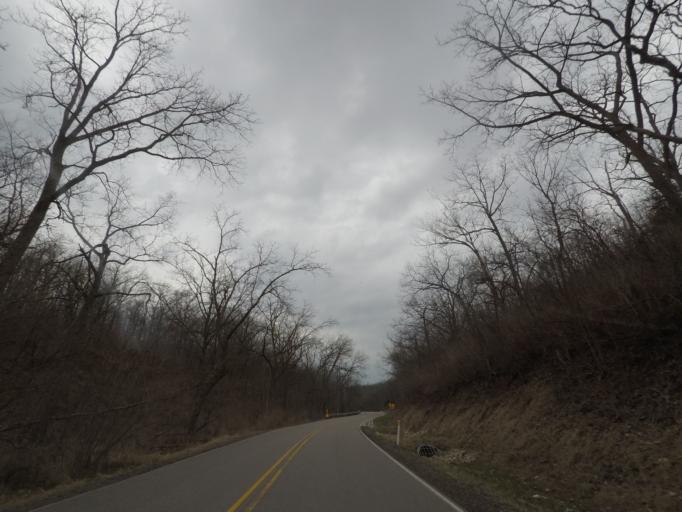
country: US
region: Wisconsin
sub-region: Dane County
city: Cross Plains
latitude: 43.1072
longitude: -89.5852
